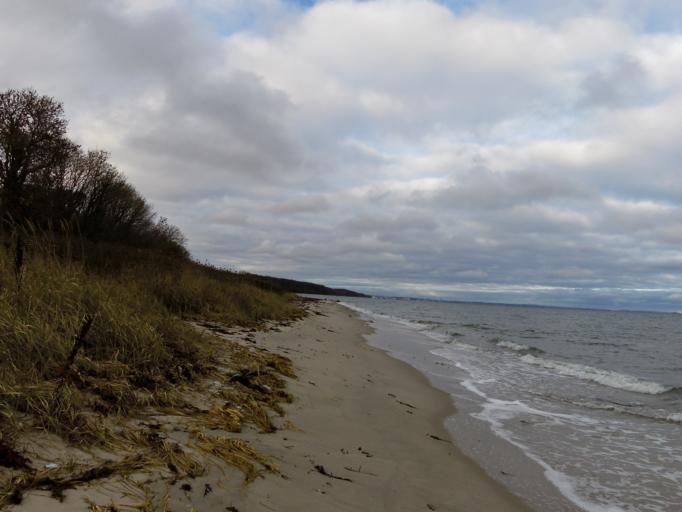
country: DK
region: Central Jutland
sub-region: Arhus Kommune
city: Beder
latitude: 56.0516
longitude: 10.2683
